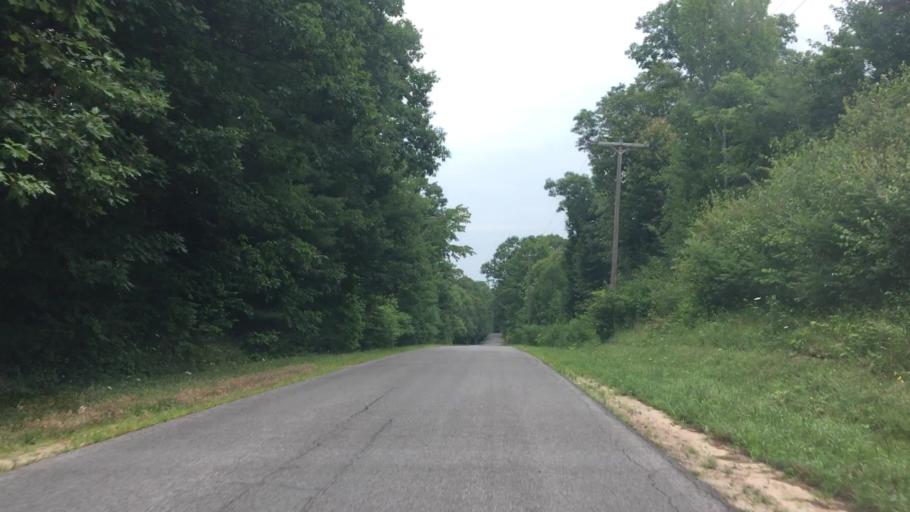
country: US
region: New York
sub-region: Clinton County
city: Peru
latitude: 44.6027
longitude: -73.6272
